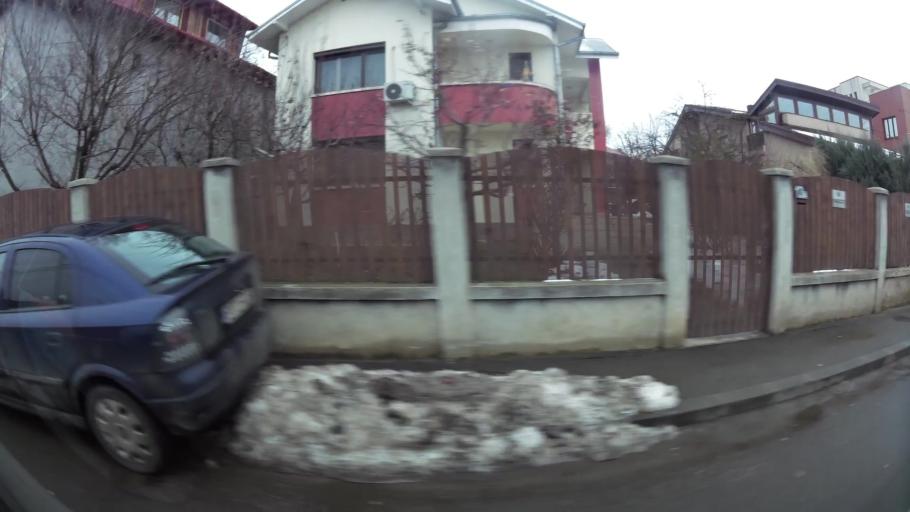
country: RO
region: Ilfov
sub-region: Comuna Popesti-Leordeni
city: Popesti-Leordeni
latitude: 44.4067
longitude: 26.1697
